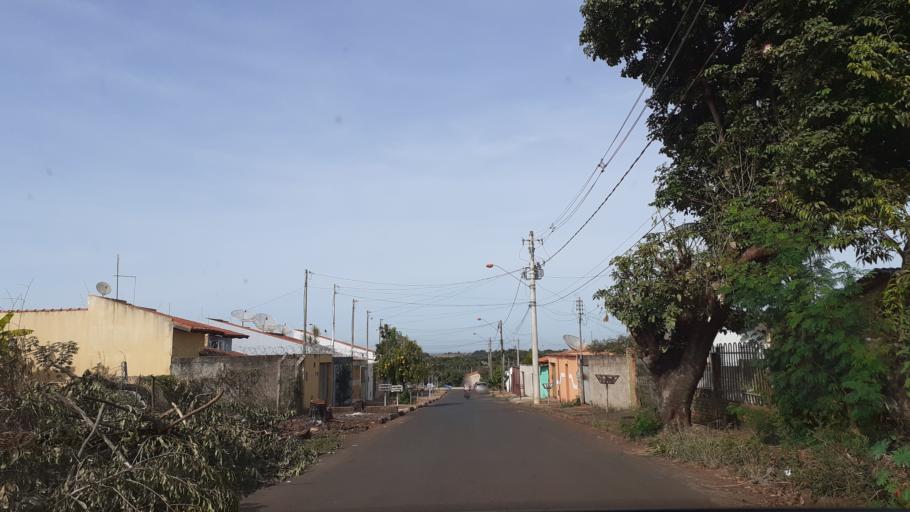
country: BR
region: Goias
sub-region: Itumbiara
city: Itumbiara
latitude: -18.4176
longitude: -49.2386
